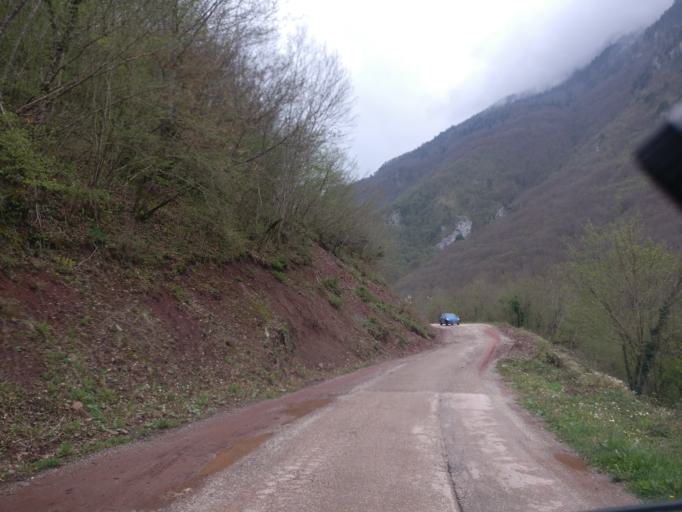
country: BA
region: Republika Srpska
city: Foca
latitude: 43.3559
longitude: 18.8173
